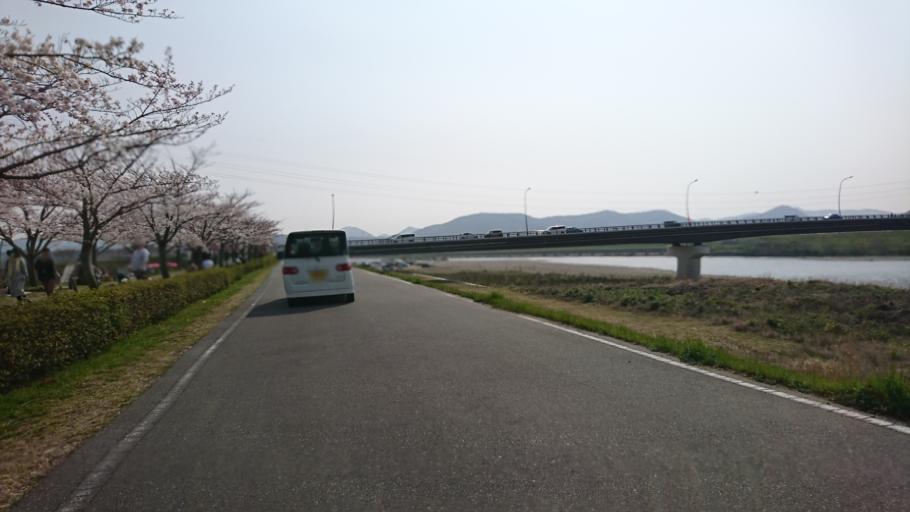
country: JP
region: Hyogo
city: Ono
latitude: 34.8624
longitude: 134.9184
